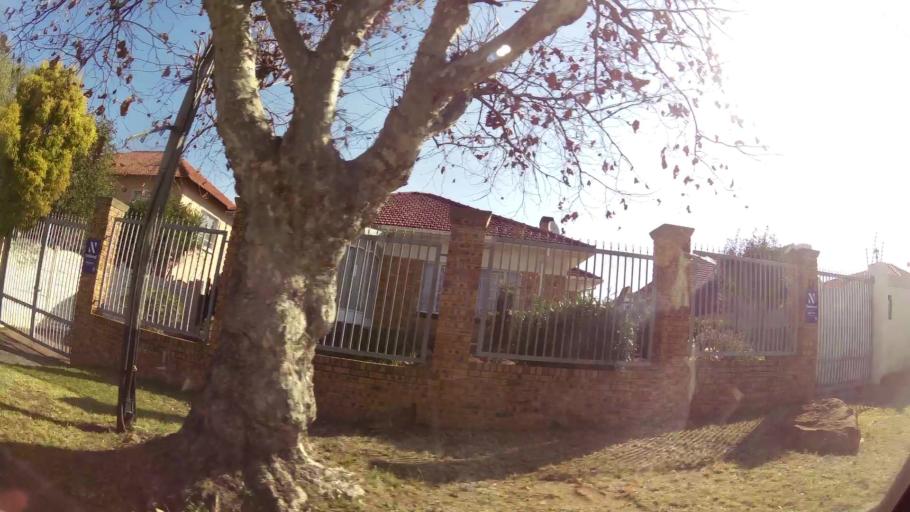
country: ZA
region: Gauteng
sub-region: City of Johannesburg Metropolitan Municipality
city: Johannesburg
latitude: -26.2587
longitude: 28.0665
